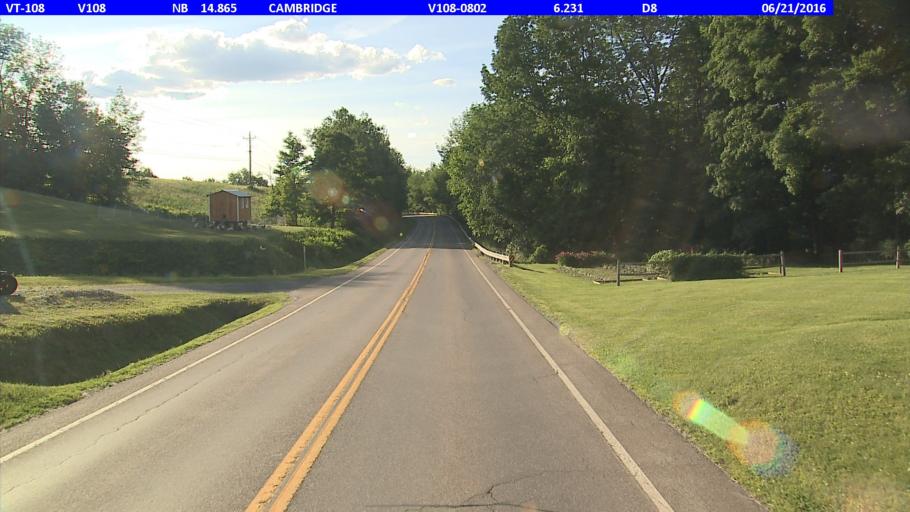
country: US
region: Vermont
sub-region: Lamoille County
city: Johnson
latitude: 44.6139
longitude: -72.8142
